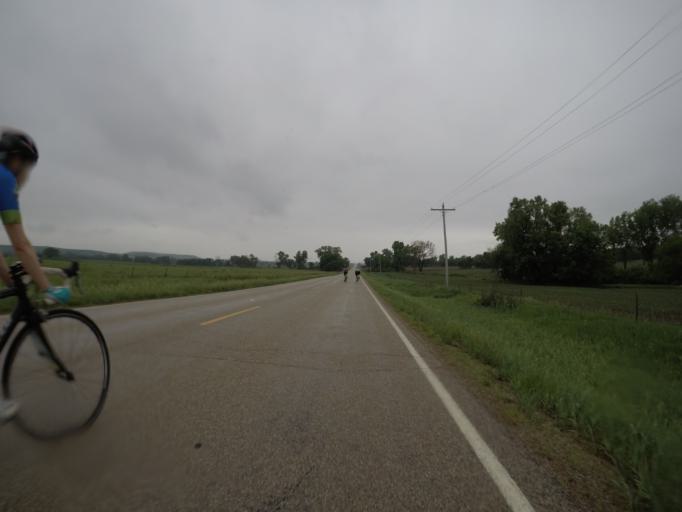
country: US
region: Kansas
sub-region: Pottawatomie County
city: Wamego
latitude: 39.3718
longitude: -96.2212
